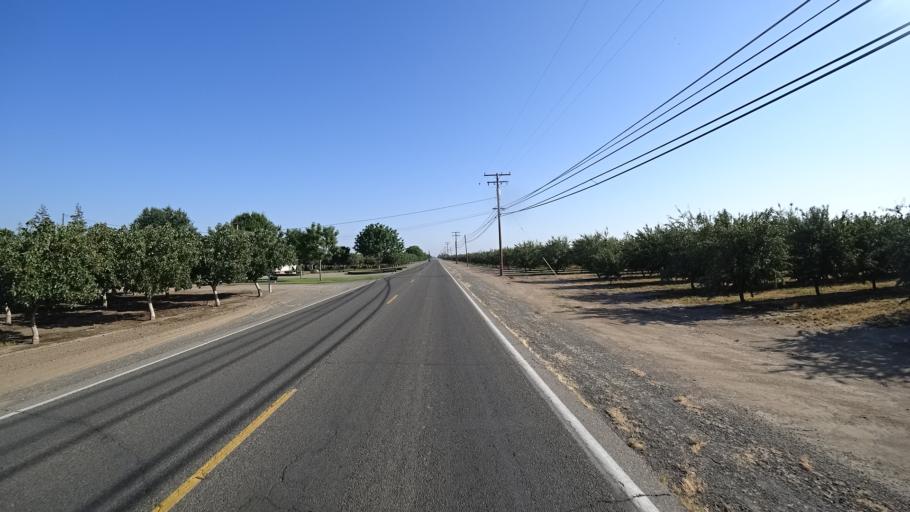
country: US
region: California
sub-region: Kings County
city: Armona
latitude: 36.3584
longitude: -119.7090
